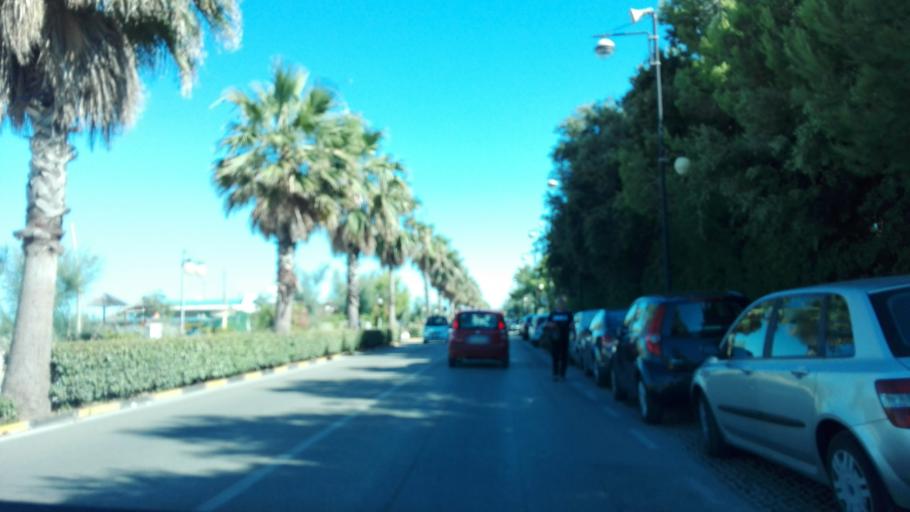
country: IT
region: Abruzzo
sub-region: Provincia di Pescara
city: Montesilvano Marina
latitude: 42.5058
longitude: 14.1729
